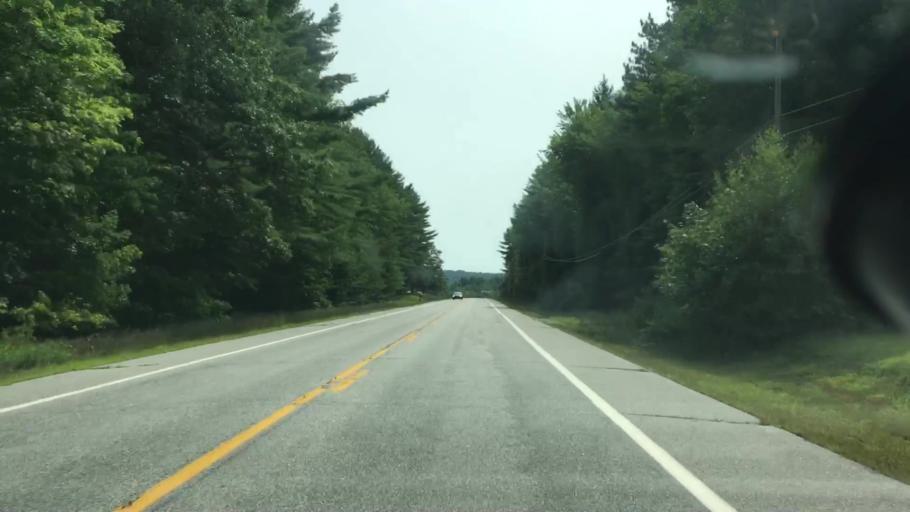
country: US
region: Maine
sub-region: Kennebec County
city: Wayne
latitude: 44.3982
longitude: -70.1215
